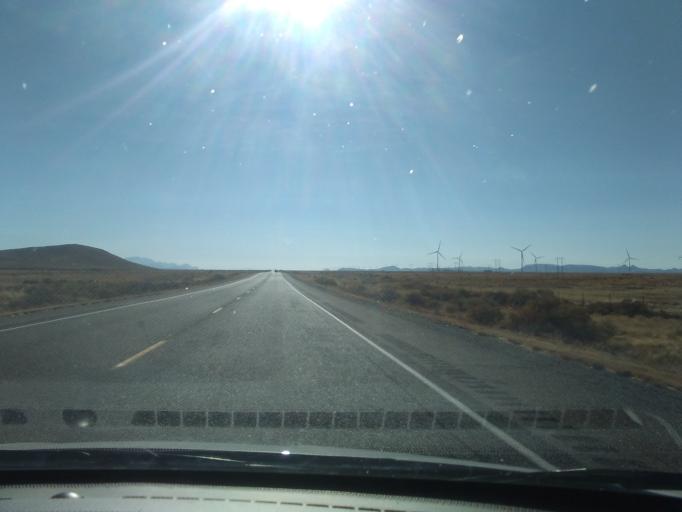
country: US
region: New Mexico
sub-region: Dona Ana County
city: Hatch
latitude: 32.5546
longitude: -107.4744
